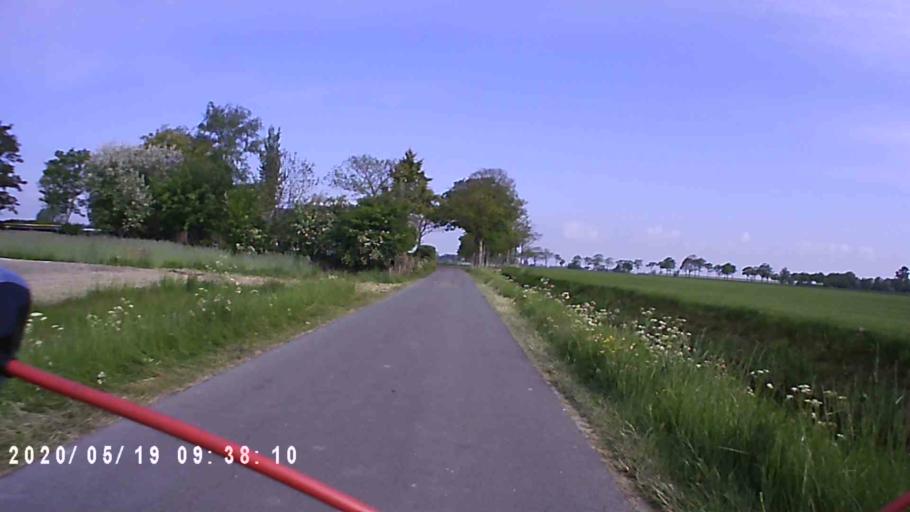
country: NL
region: Groningen
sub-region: Gemeente Zuidhorn
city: Grijpskerk
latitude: 53.2899
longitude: 6.2848
